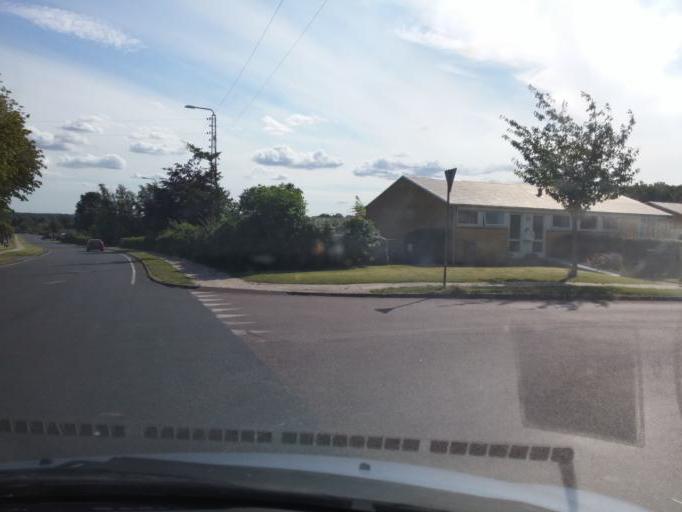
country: DK
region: South Denmark
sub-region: Kerteminde Kommune
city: Munkebo
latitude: 55.4651
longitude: 10.5636
